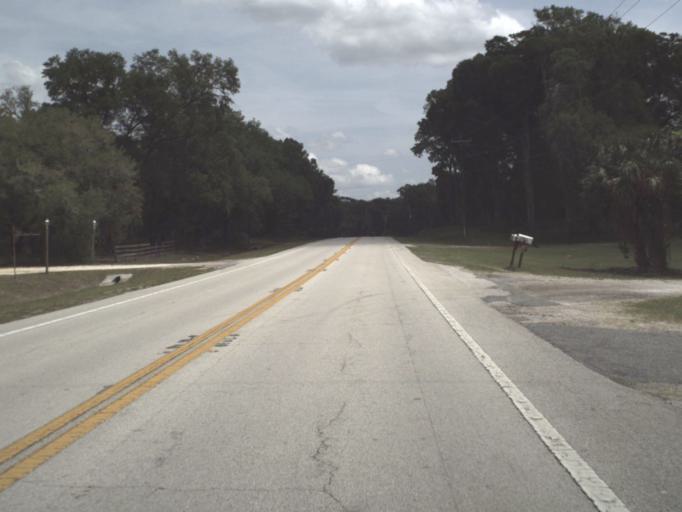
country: US
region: Florida
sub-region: Lake County
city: Mount Plymouth
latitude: 28.8881
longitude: -81.4716
